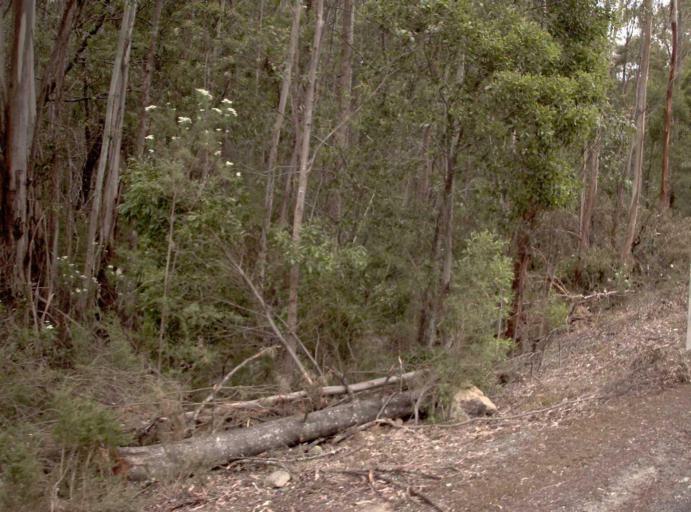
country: AU
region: New South Wales
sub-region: Bombala
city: Bombala
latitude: -37.2809
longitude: 149.2232
